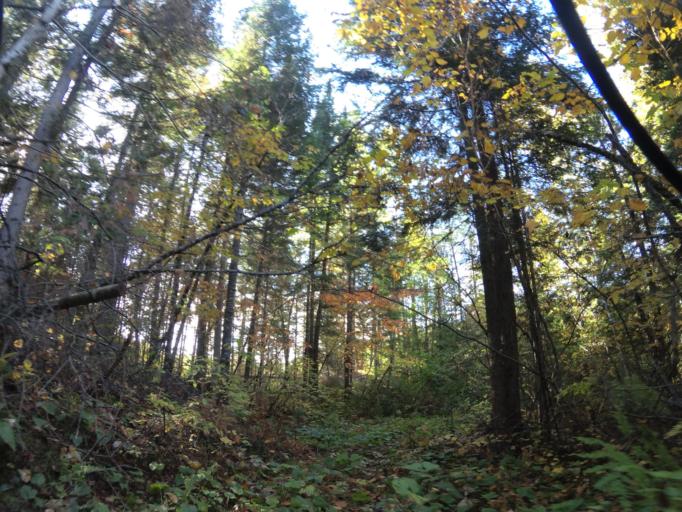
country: CA
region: Ontario
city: Pembroke
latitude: 45.3381
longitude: -77.1649
